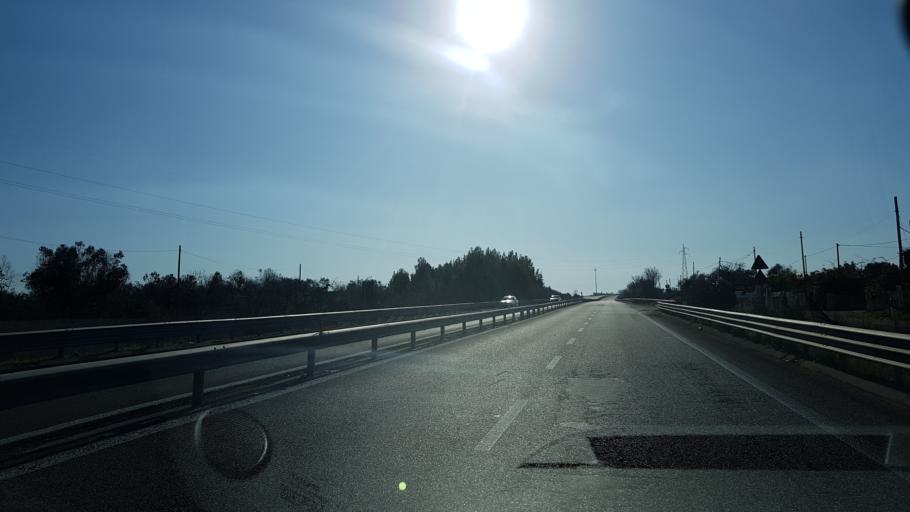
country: IT
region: Apulia
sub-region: Provincia di Lecce
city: Galatone
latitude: 40.1348
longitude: 18.0518
